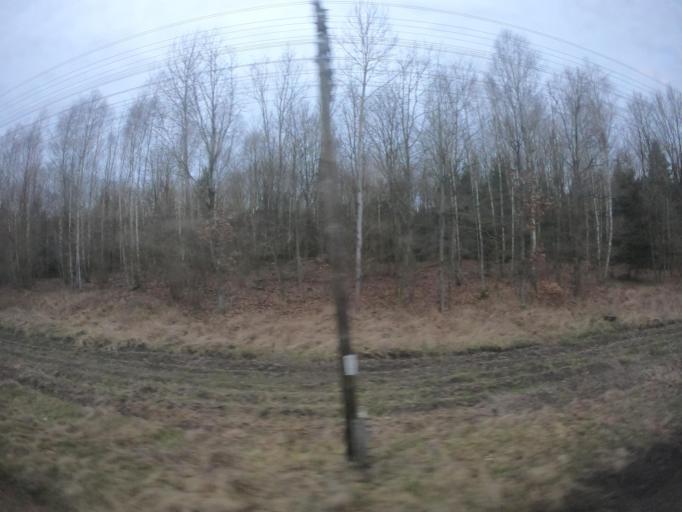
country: PL
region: West Pomeranian Voivodeship
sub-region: Powiat szczecinecki
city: Borne Sulinowo
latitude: 53.6521
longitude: 16.5379
